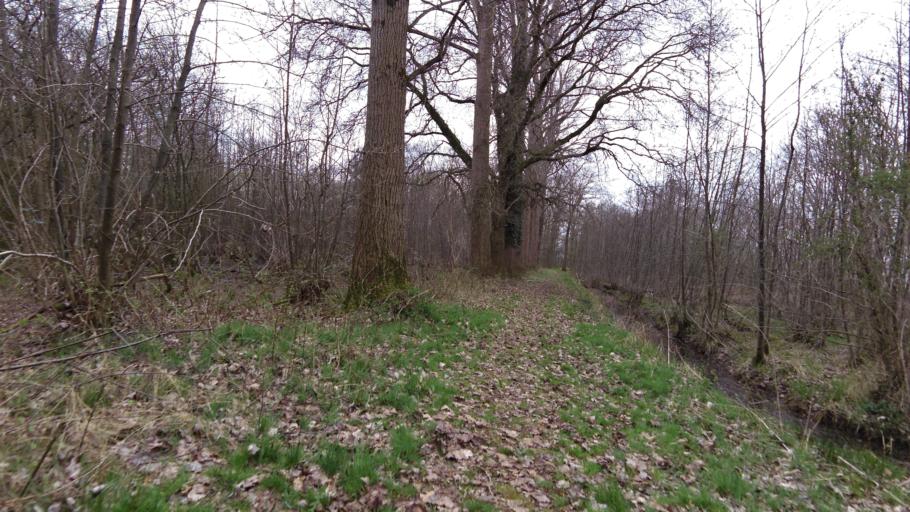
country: NL
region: Gelderland
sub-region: Gemeente Barneveld
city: Zwartebroek
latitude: 52.1947
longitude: 5.4919
